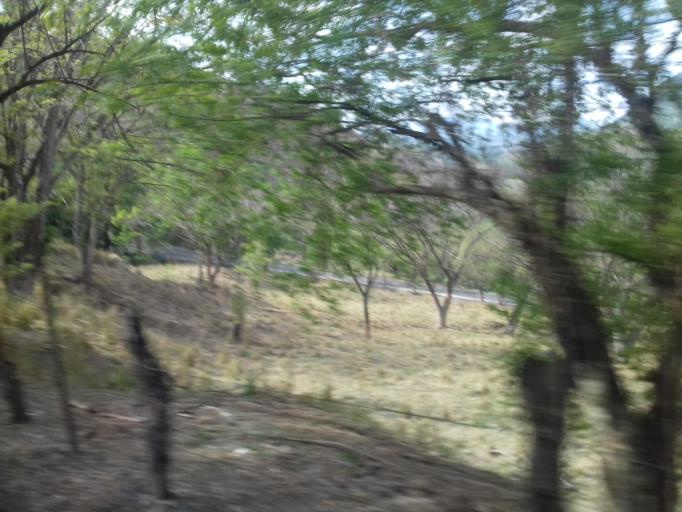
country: CO
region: Antioquia
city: Titiribi
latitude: 5.9794
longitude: -75.8268
